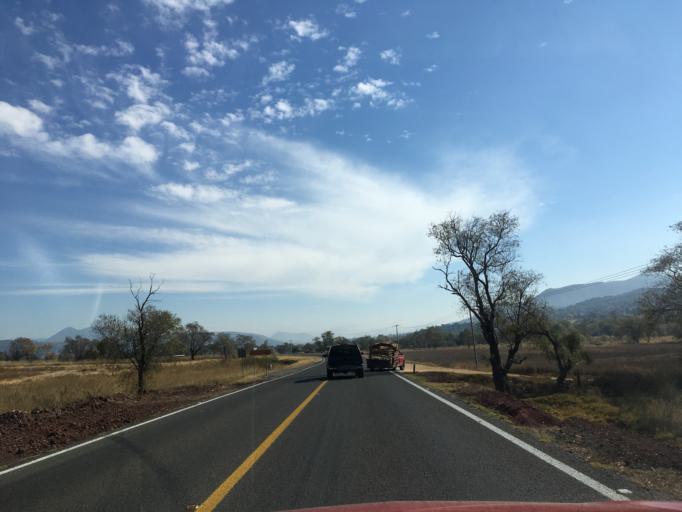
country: MX
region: Michoacan
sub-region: Hidalgo
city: San Lucas Huarirapeo (La Mesa de San Lucas)
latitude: 19.6810
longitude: -100.6422
